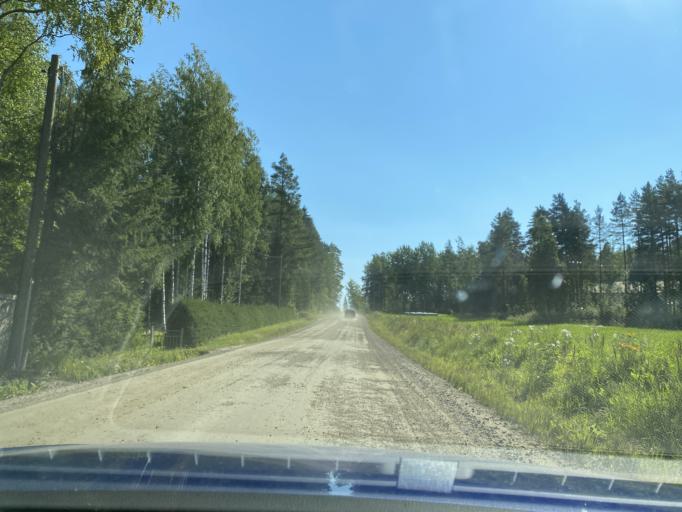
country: FI
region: Central Finland
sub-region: Jyvaeskylae
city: Korpilahti
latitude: 61.8887
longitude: 25.4032
